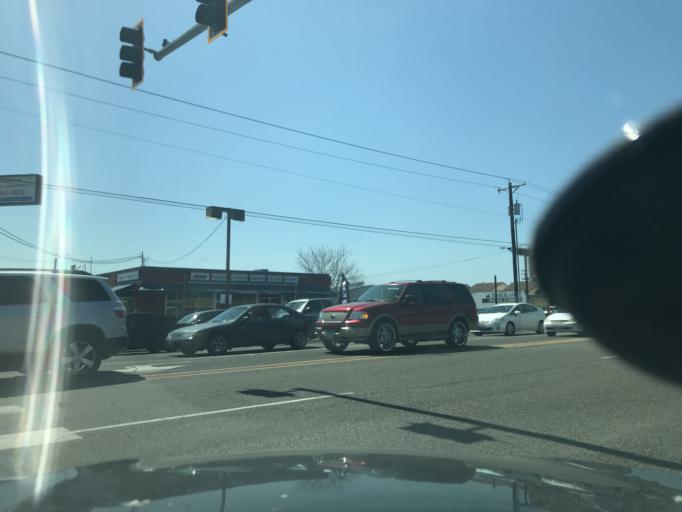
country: US
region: Oregon
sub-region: Multnomah County
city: Gresham
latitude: 45.5047
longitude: -122.4758
